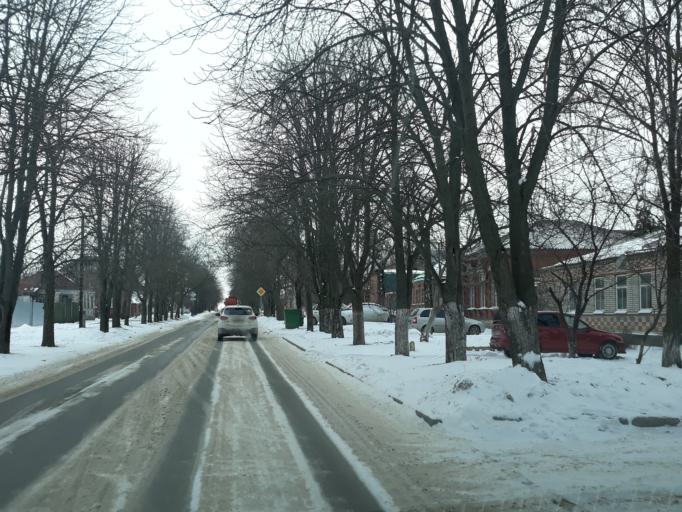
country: RU
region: Rostov
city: Taganrog
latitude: 47.2049
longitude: 38.9201
